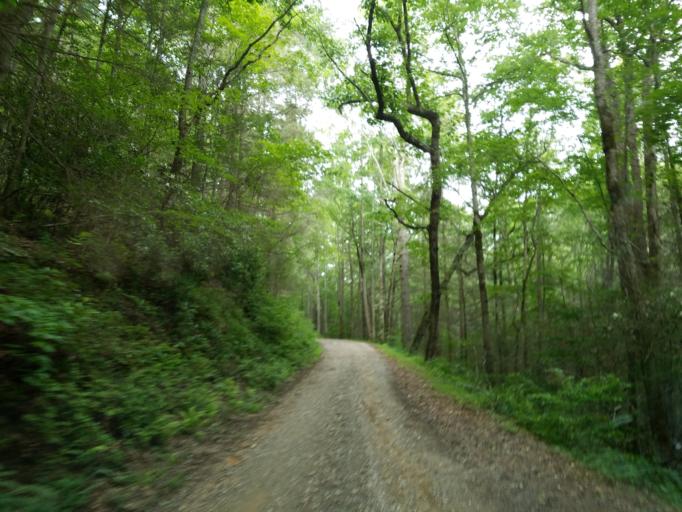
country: US
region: Georgia
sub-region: Union County
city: Blairsville
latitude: 34.7709
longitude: -84.0618
